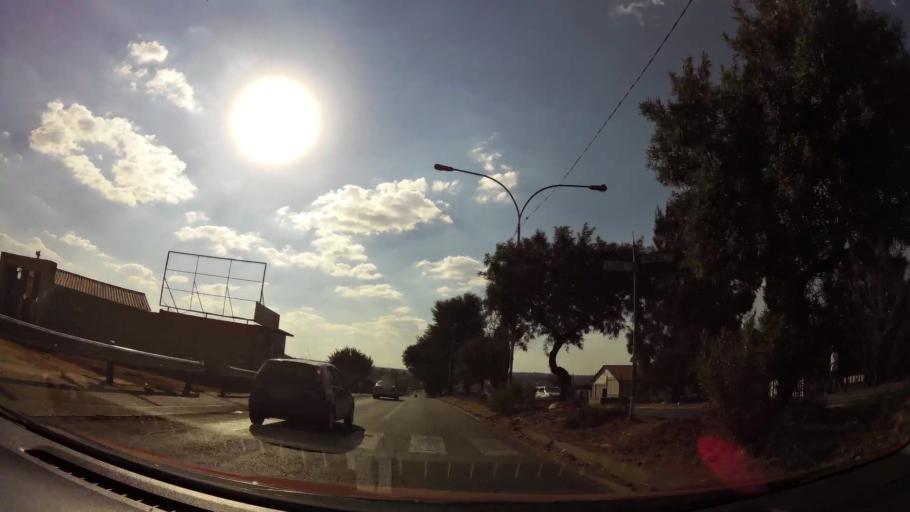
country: ZA
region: Gauteng
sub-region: City of Johannesburg Metropolitan Municipality
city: Soweto
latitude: -26.2248
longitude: 27.8729
